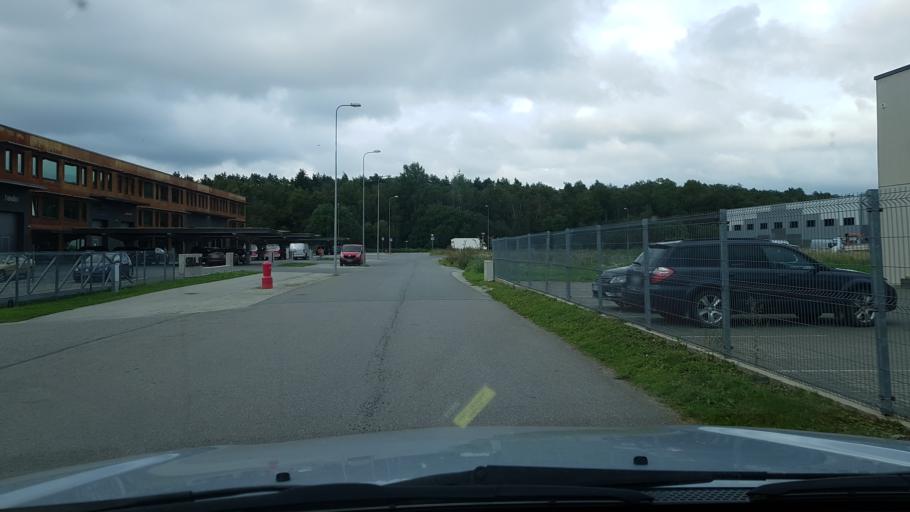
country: EE
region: Harju
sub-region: Tallinna linn
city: Kose
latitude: 59.3995
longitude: 24.8261
